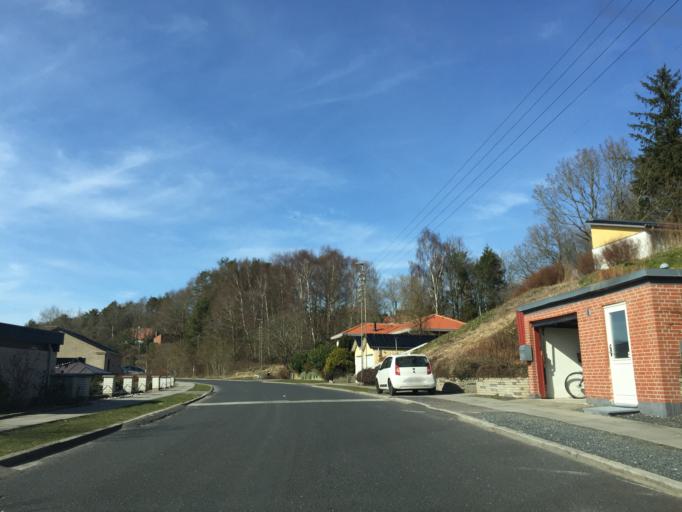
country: DK
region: Central Jutland
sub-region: Silkeborg Kommune
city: Silkeborg
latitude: 56.1900
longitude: 9.5417
